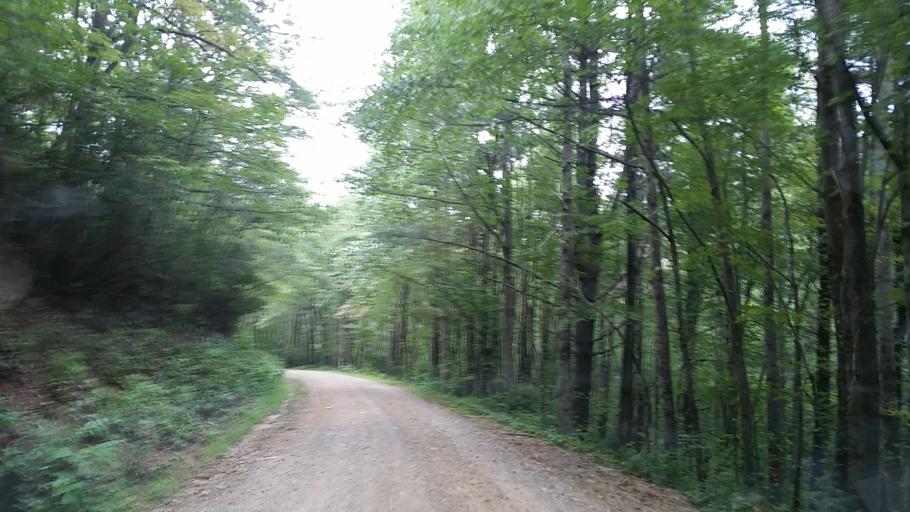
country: US
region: Georgia
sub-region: Lumpkin County
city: Dahlonega
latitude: 34.6509
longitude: -84.0653
